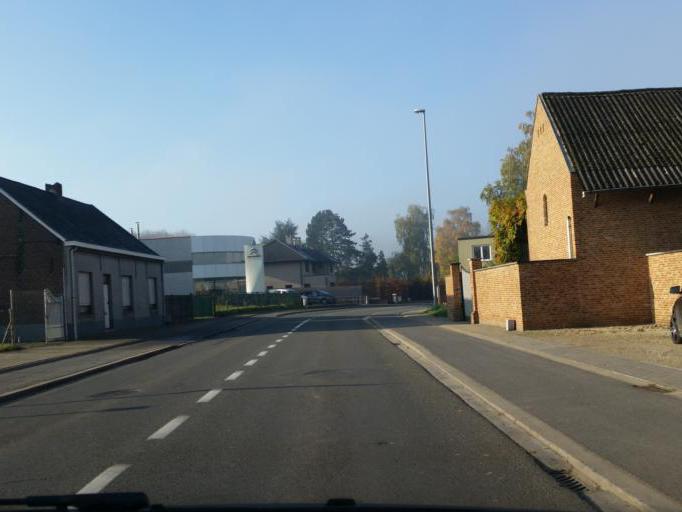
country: BE
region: Flanders
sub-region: Provincie Vlaams-Brabant
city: Opwijk
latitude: 50.9514
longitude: 4.1338
